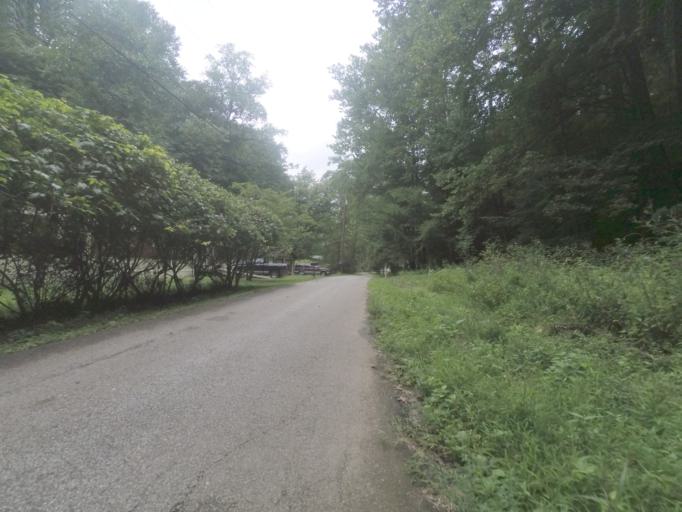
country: US
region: West Virginia
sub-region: Cabell County
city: Huntington
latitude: 38.3856
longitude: -82.4332
